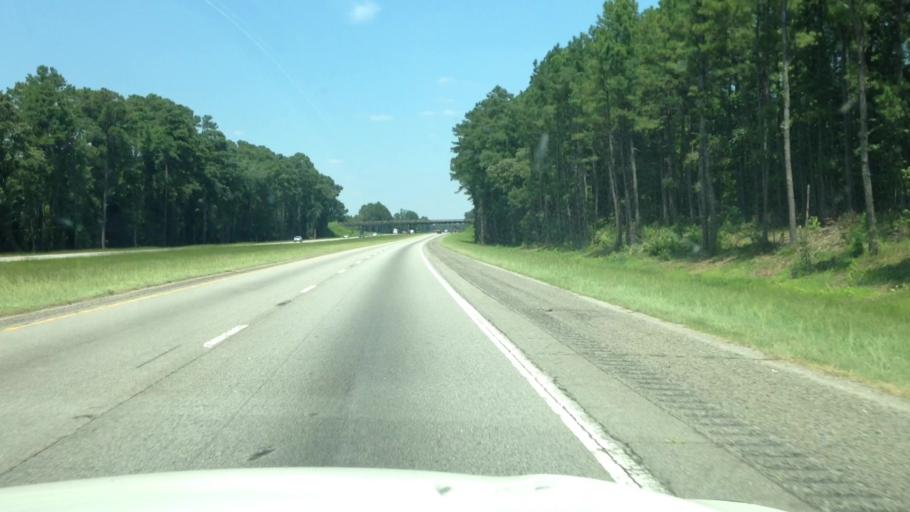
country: US
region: South Carolina
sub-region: Dillon County
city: Dillon
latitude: 34.4764
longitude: -79.3421
